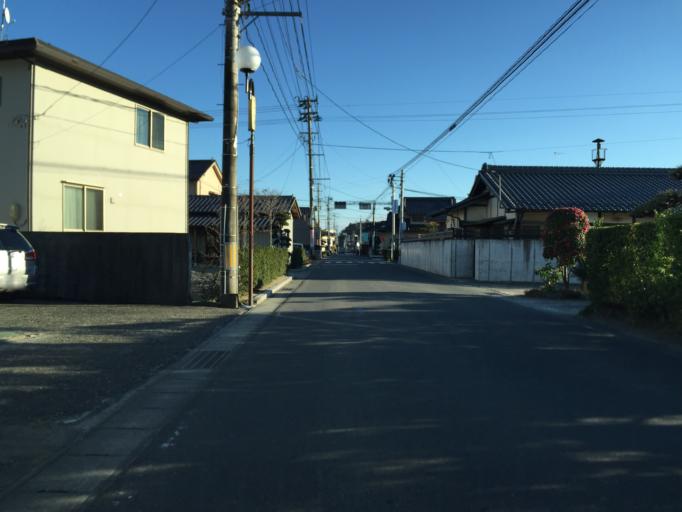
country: JP
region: Fukushima
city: Iwaki
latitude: 37.0824
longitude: 140.8665
